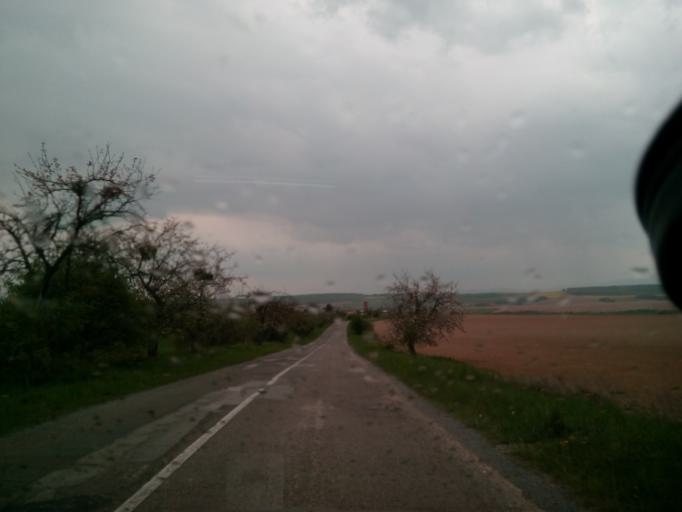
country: SK
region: Kosicky
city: Kosice
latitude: 48.7478
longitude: 21.4548
